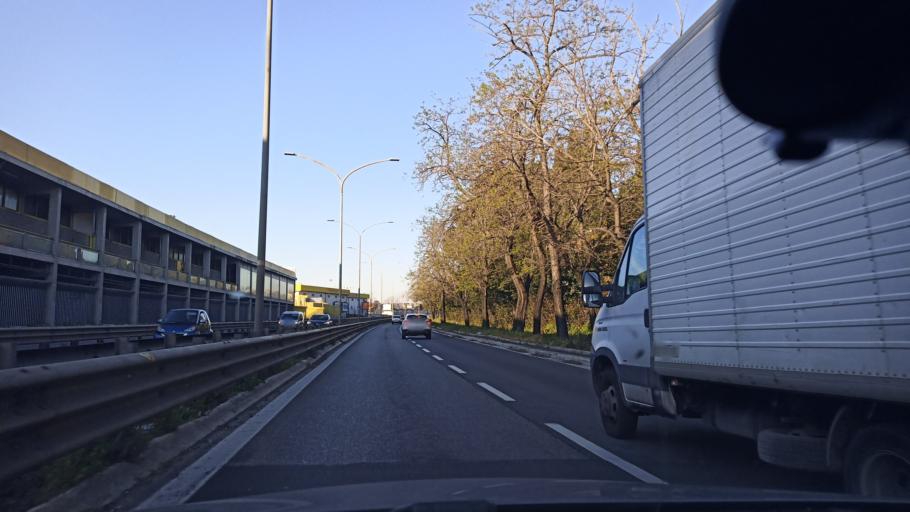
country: IT
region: Latium
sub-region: Citta metropolitana di Roma Capitale
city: Rome
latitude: 41.8991
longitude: 12.5277
